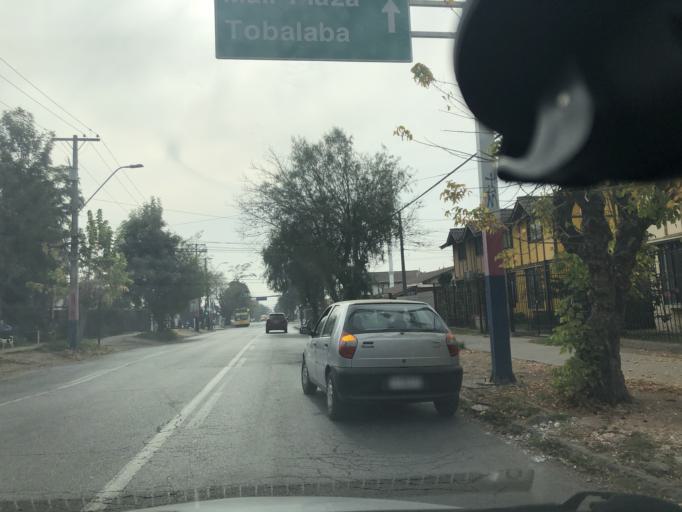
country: CL
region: Santiago Metropolitan
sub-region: Provincia de Cordillera
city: Puente Alto
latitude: -33.5777
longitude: -70.5697
